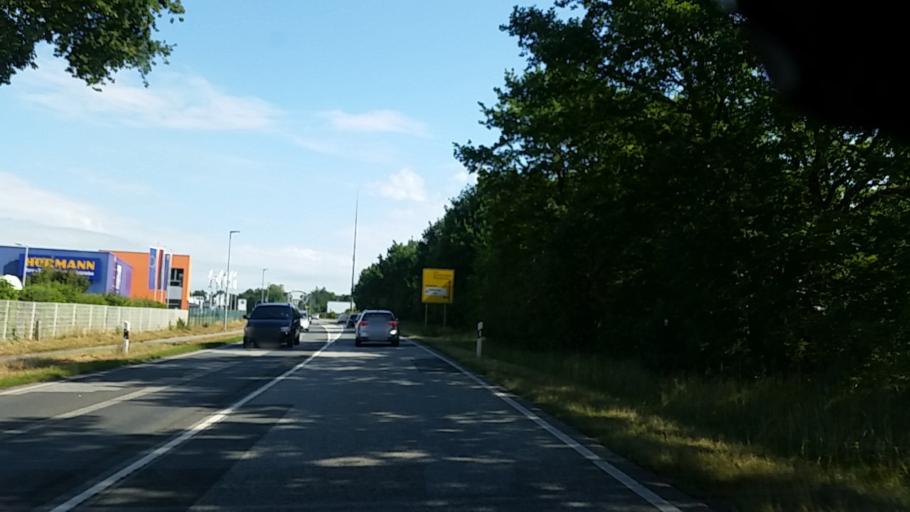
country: DE
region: Schleswig-Holstein
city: Oersdorf
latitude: 53.8254
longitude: 9.9731
